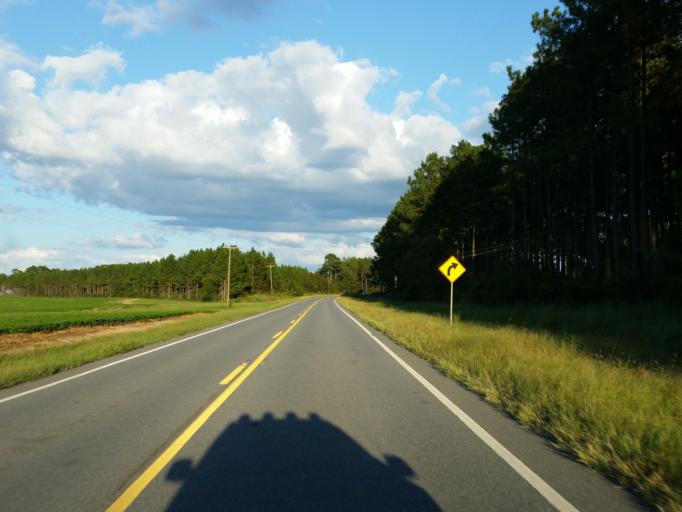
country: US
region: Georgia
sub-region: Dooly County
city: Vienna
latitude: 32.0861
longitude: -83.7191
